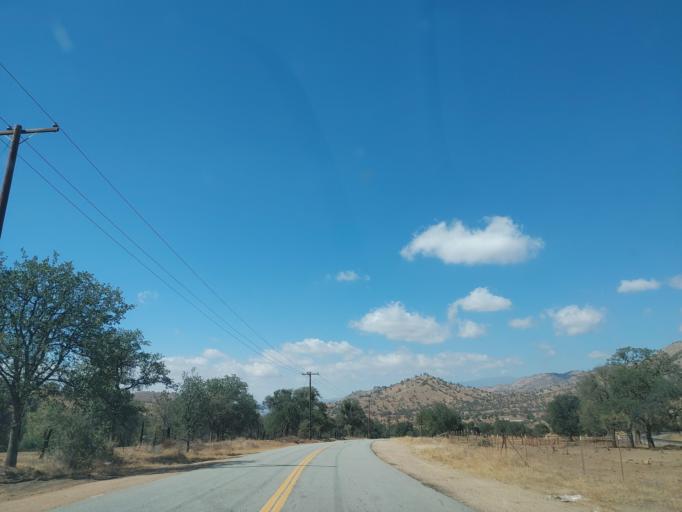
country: US
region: California
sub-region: Kern County
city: Golden Hills
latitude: 35.2007
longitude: -118.5416
